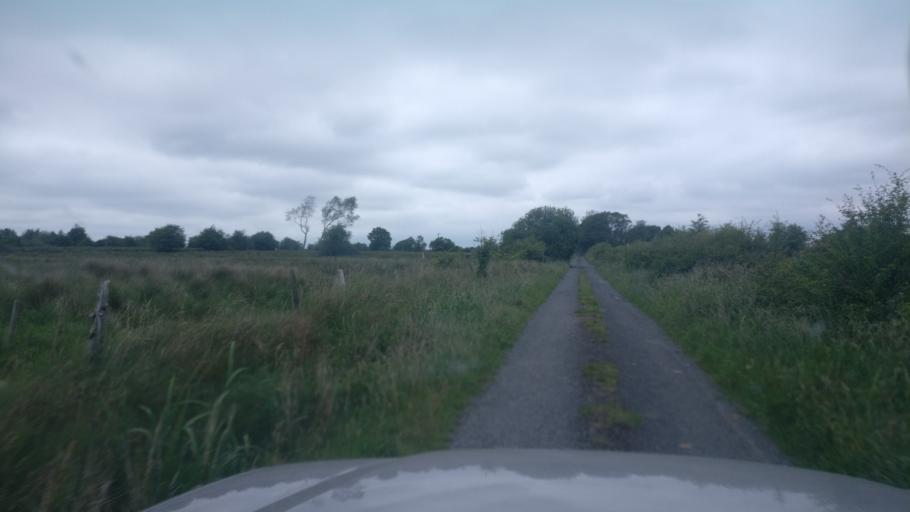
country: IE
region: Connaught
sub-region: County Galway
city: Ballinasloe
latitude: 53.2999
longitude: -8.3618
